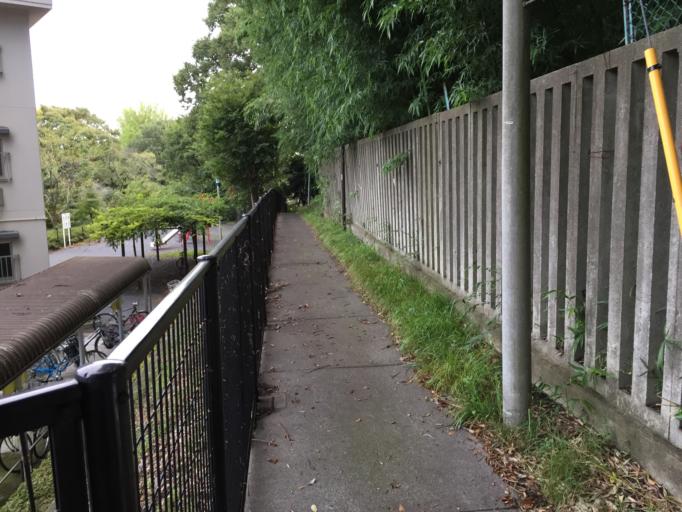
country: JP
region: Tokyo
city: Kokubunji
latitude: 35.6667
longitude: 139.4798
